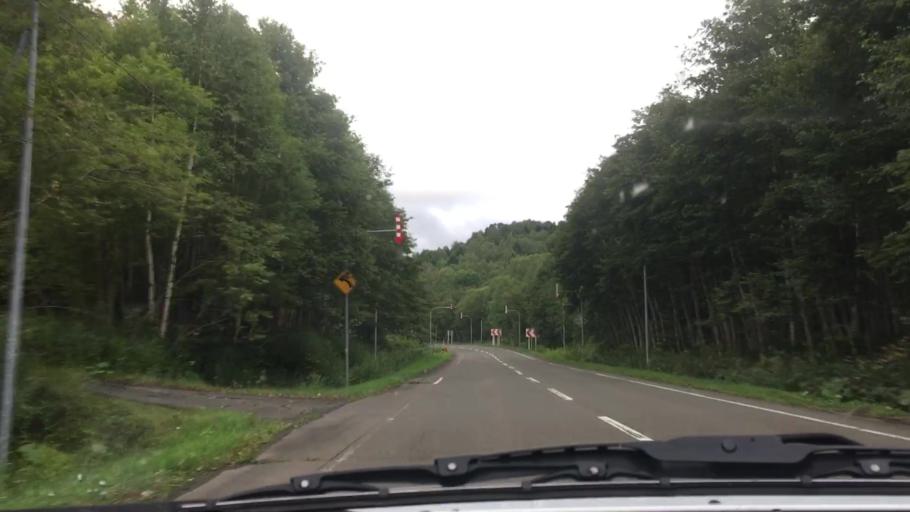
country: JP
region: Hokkaido
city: Shimo-furano
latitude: 43.0616
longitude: 142.6686
